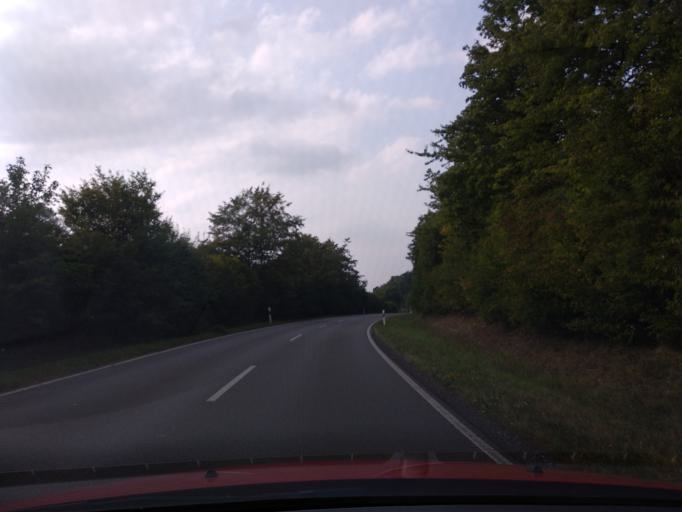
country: DE
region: Hesse
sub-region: Regierungsbezirk Kassel
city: Calden
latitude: 51.3791
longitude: 9.3711
